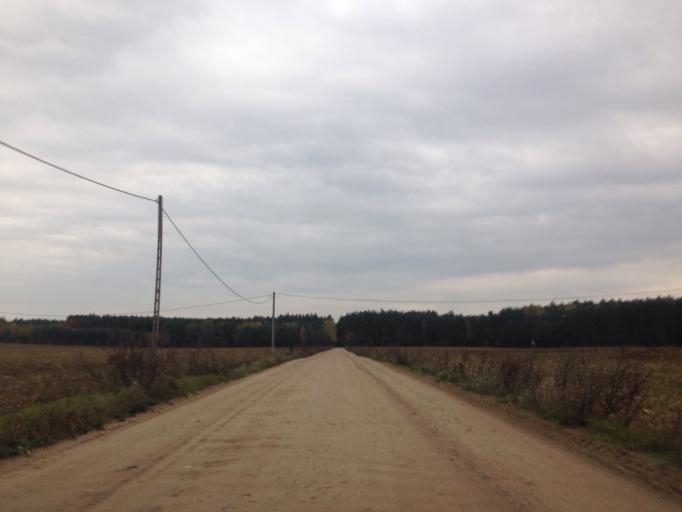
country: PL
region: Kujawsko-Pomorskie
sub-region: Powiat brodnicki
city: Brzozie
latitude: 53.2943
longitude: 19.5740
